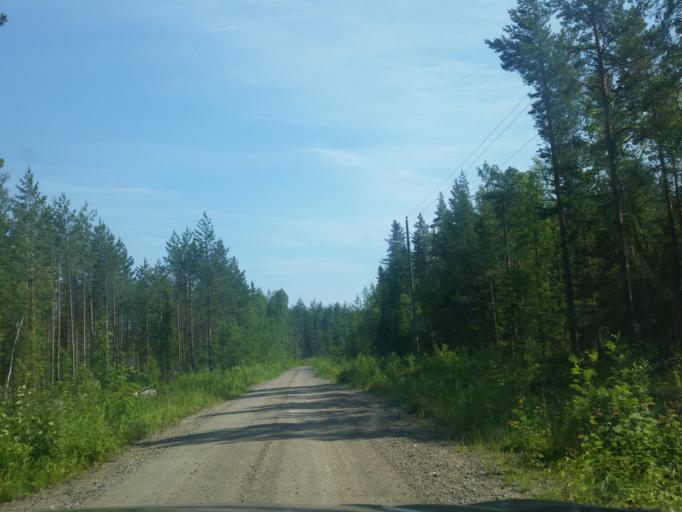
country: FI
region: Northern Savo
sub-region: Sisae-Savo
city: Tervo
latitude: 63.0814
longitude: 26.5843
